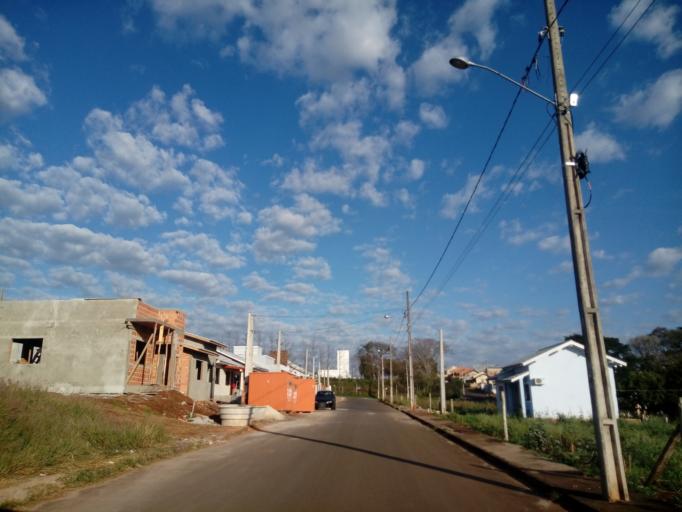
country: BR
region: Santa Catarina
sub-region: Chapeco
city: Chapeco
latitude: -27.1088
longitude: -52.6678
